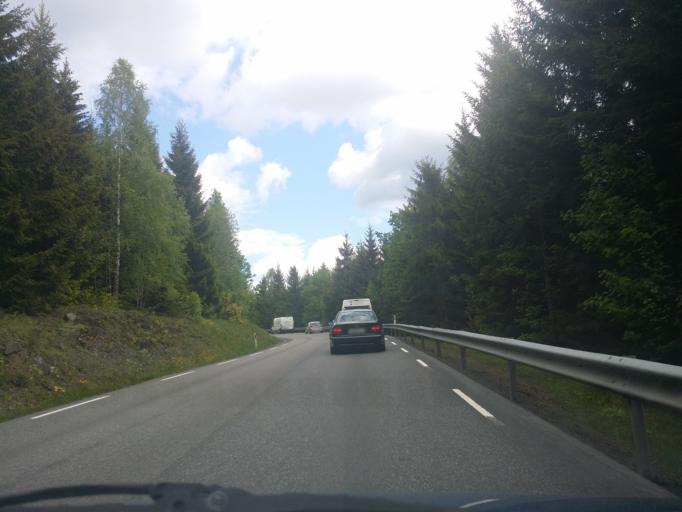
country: NO
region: Oppland
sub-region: Jevnaker
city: Jevnaker
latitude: 60.2628
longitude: 10.4511
